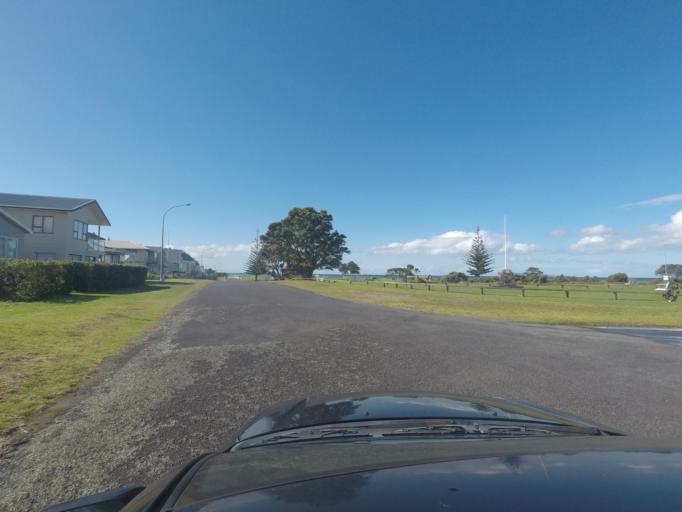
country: NZ
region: Bay of Plenty
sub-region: Western Bay of Plenty District
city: Waihi Beach
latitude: -37.4019
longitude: 175.9387
